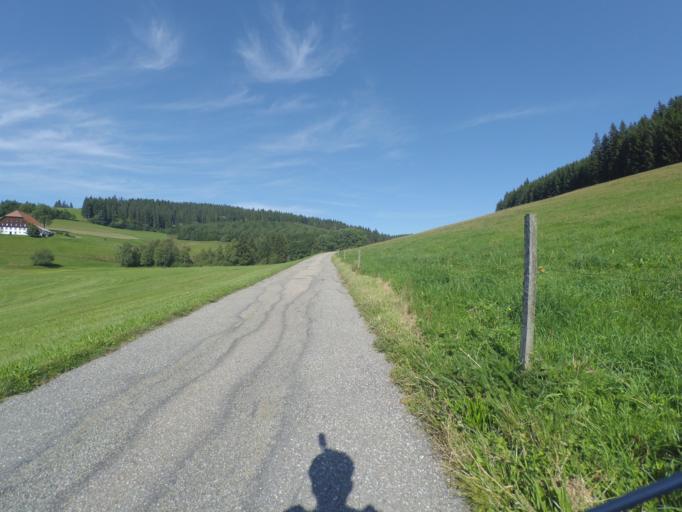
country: DE
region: Baden-Wuerttemberg
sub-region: Freiburg Region
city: Breitnau
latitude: 47.9569
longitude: 8.1318
